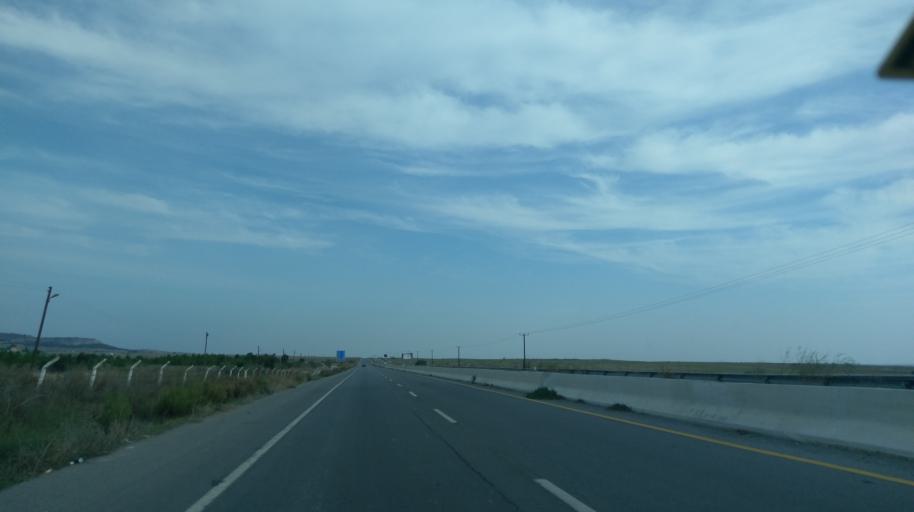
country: CY
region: Lefkosia
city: Mammari
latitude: 35.2145
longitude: 33.1859
